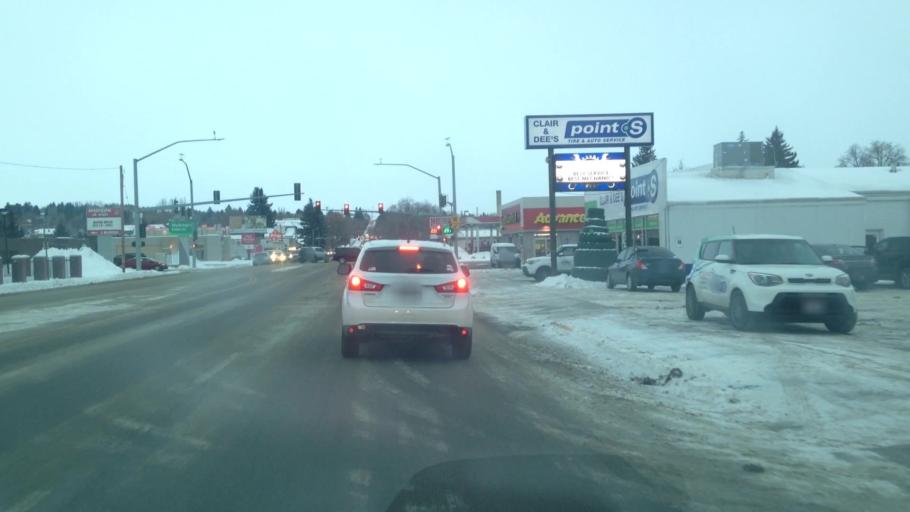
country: US
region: Idaho
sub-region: Madison County
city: Rexburg
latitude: 43.8292
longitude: -111.7782
